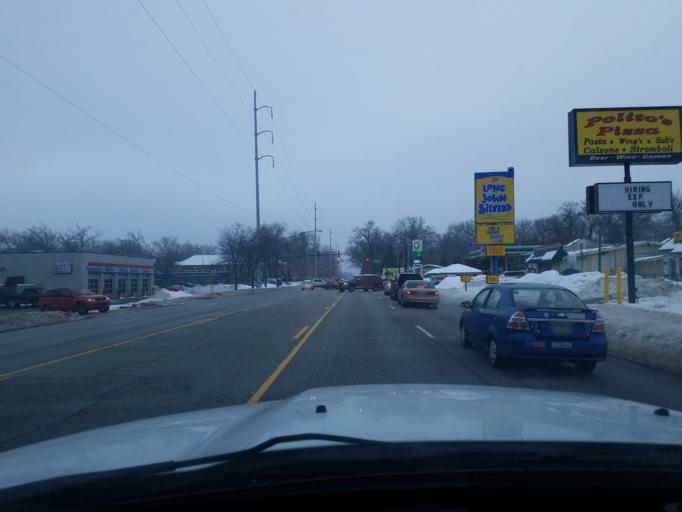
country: US
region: Indiana
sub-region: Saint Joseph County
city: Mishawaka
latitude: 41.6811
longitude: -86.1966
